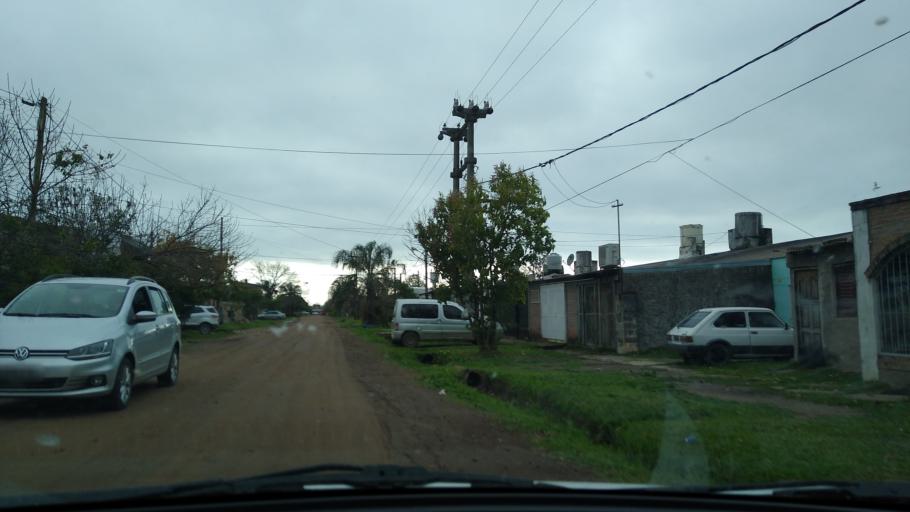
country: AR
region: Chaco
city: Resistencia
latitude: -27.4890
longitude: -58.9787
